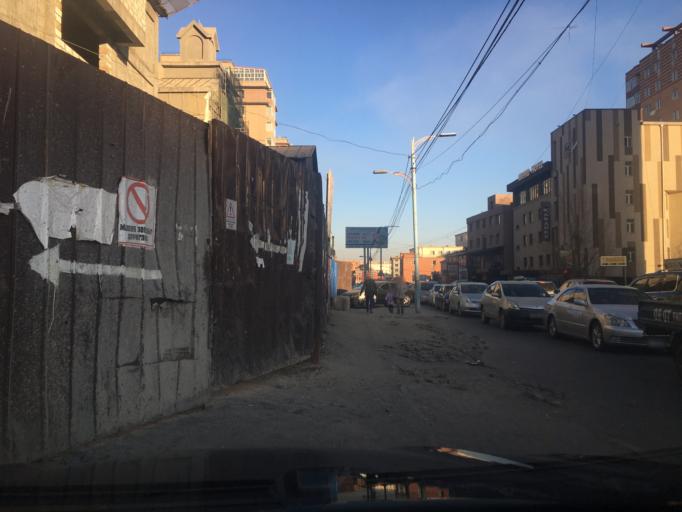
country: MN
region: Ulaanbaatar
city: Ulaanbaatar
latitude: 47.9185
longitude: 106.8867
